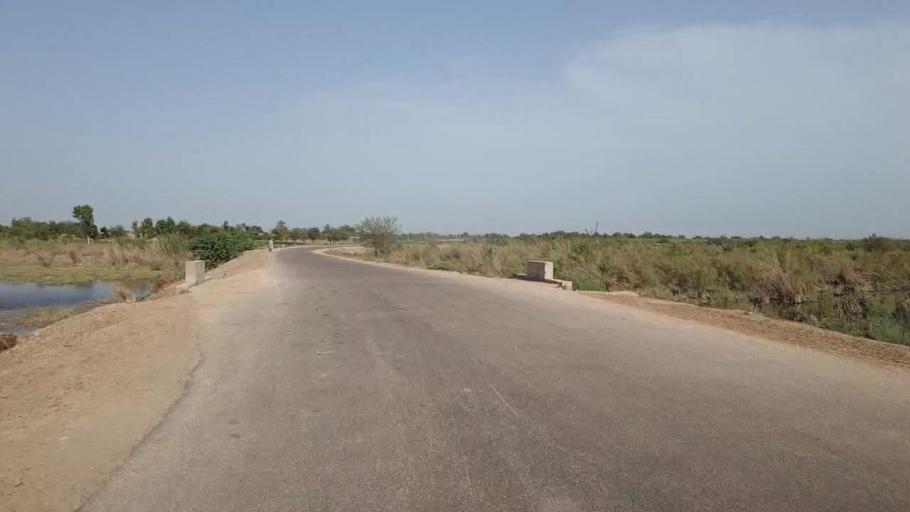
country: PK
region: Sindh
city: Sakrand
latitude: 26.2728
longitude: 68.2726
